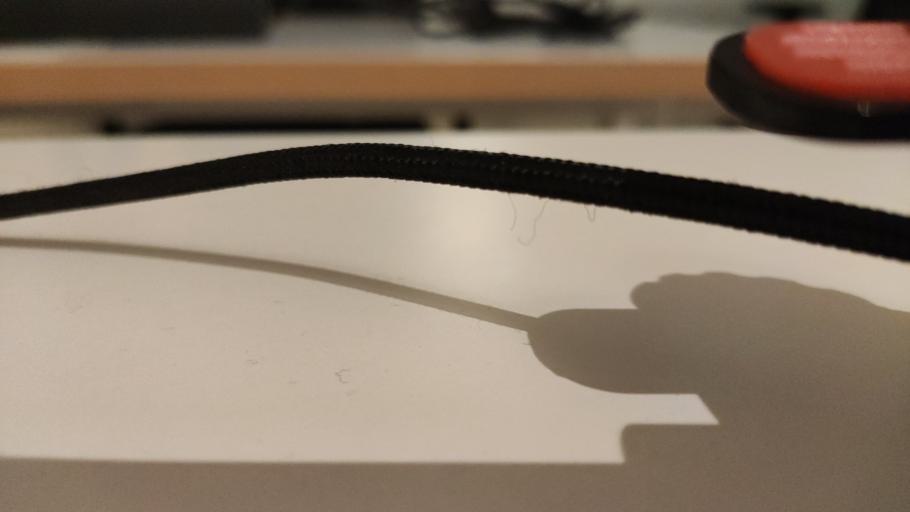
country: RU
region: Moskovskaya
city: Shemetovo
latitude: 56.4100
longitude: 37.9980
